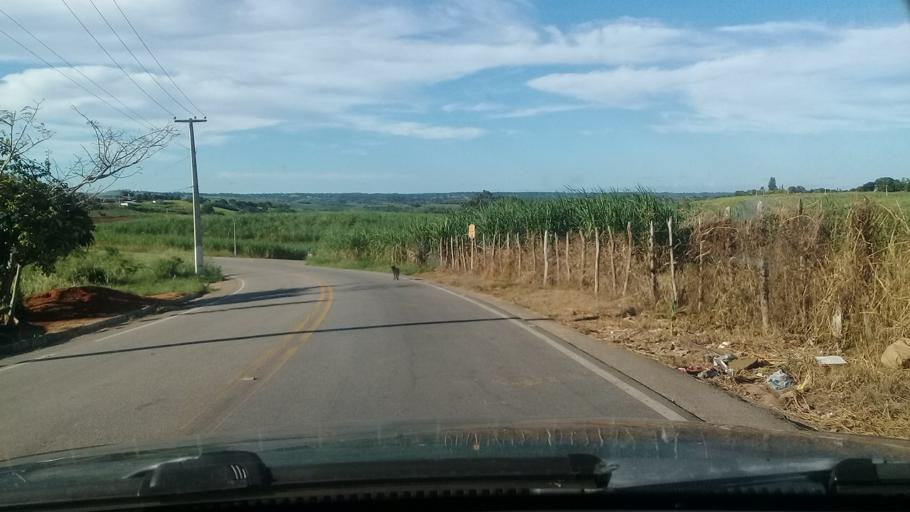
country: BR
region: Pernambuco
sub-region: Gloria Do Goita
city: Gloria do Goita
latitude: -7.9903
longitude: -35.2051
